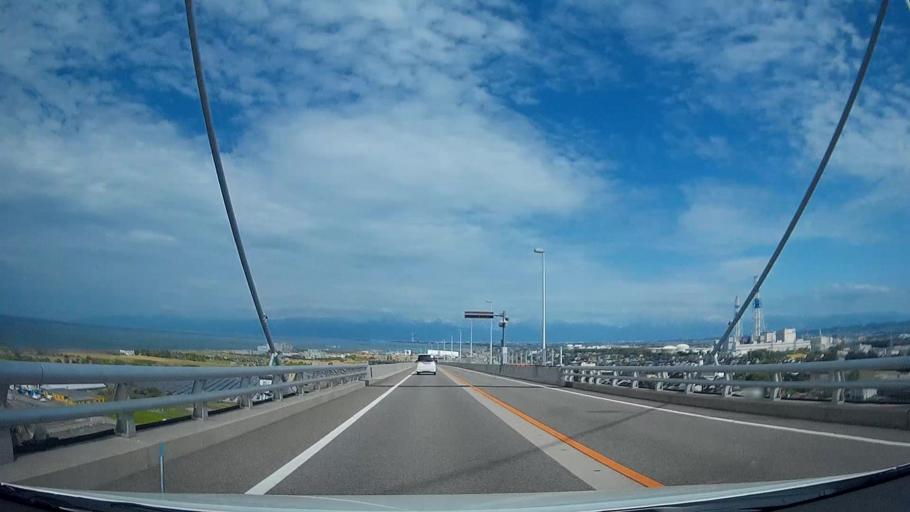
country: JP
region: Toyama
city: Nishishinminato
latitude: 36.7754
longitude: 137.1185
